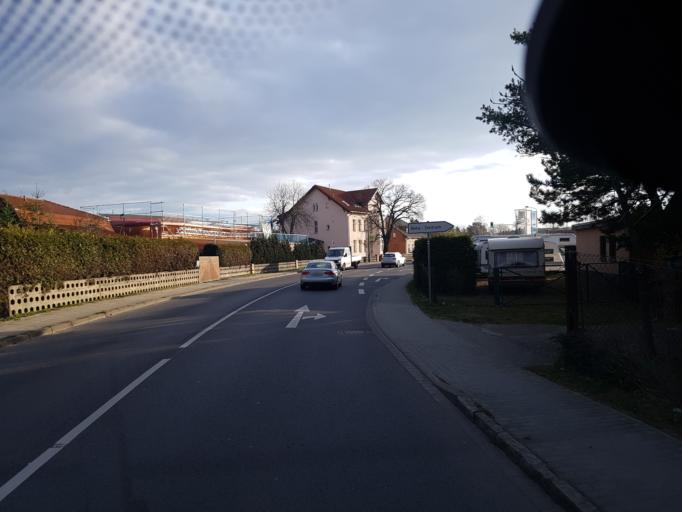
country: DE
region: Brandenburg
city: Luebben
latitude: 51.9426
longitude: 13.9116
